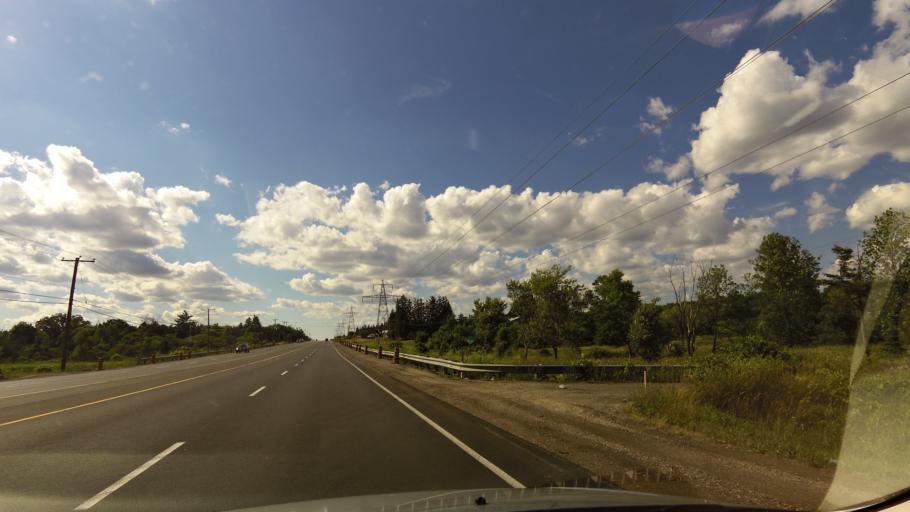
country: CA
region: Ontario
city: Ancaster
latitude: 43.3796
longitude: -80.0094
